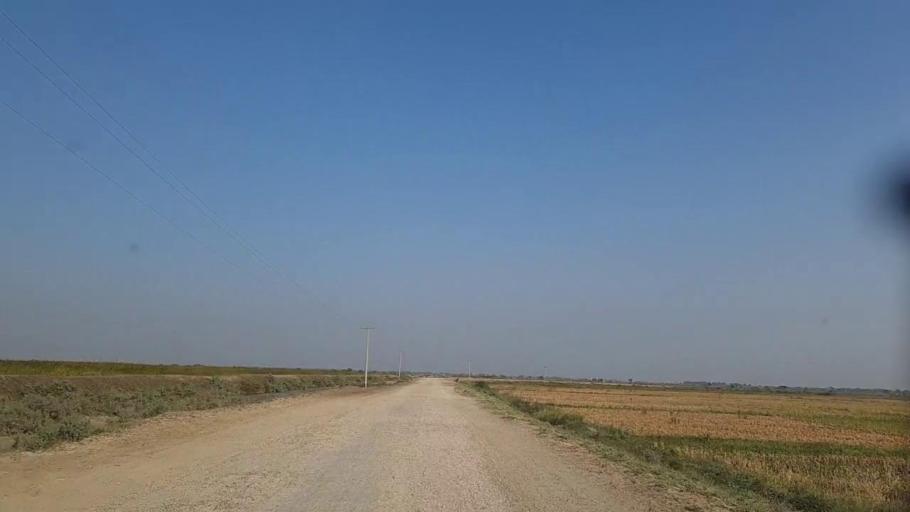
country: PK
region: Sindh
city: Jati
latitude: 24.4615
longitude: 68.2798
